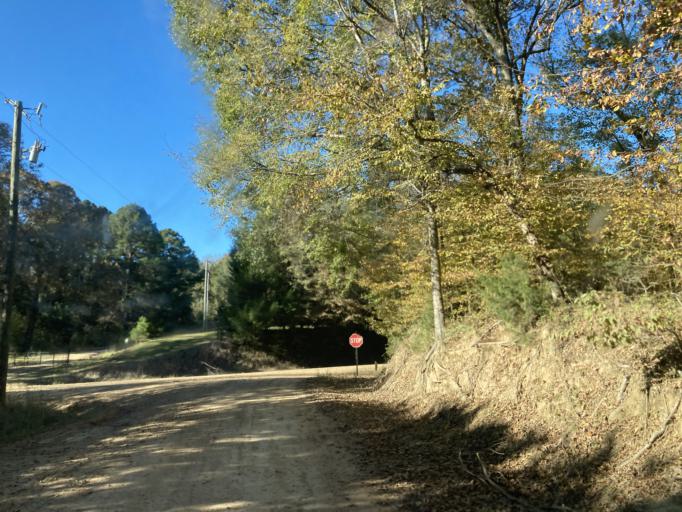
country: US
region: Mississippi
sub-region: Yazoo County
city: Yazoo City
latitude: 32.7383
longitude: -90.4392
